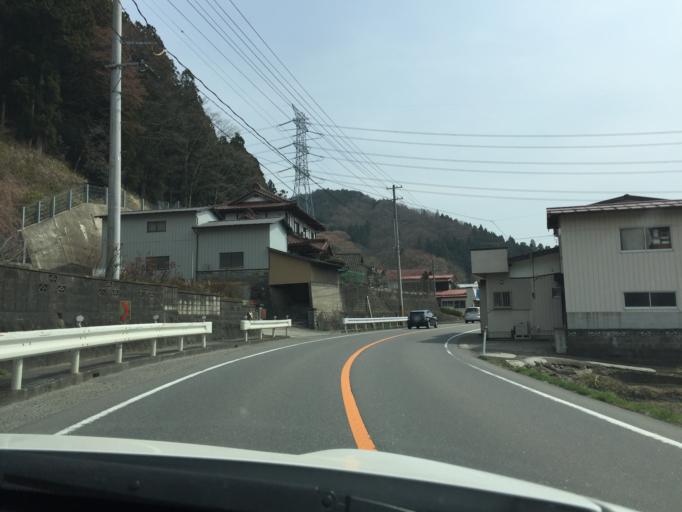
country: JP
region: Fukushima
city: Ishikawa
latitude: 37.1209
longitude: 140.5035
